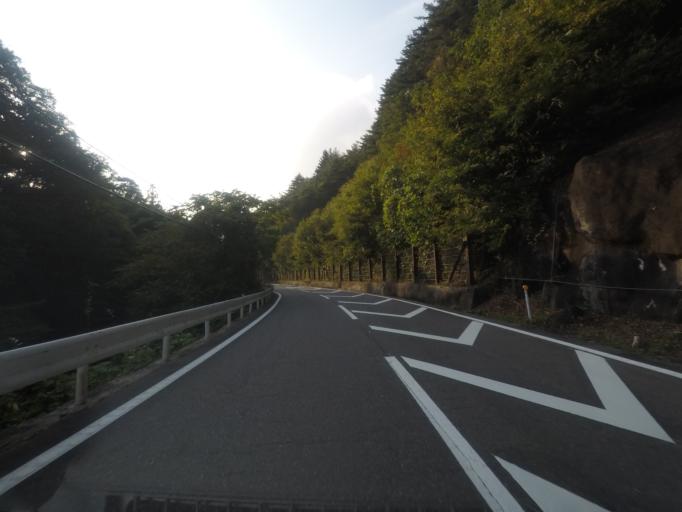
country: JP
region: Fukushima
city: Funehikimachi-funehiki
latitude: 37.5549
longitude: 140.7803
